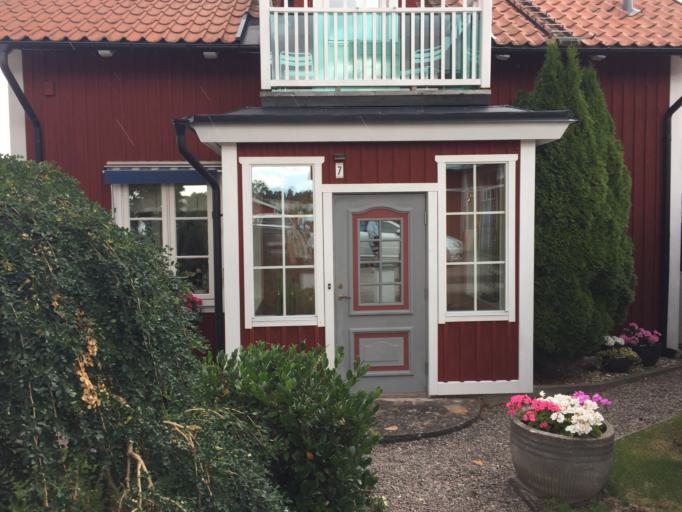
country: SE
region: OEstergoetland
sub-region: Motala Kommun
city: Borensberg
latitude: 58.5603
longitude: 15.2842
